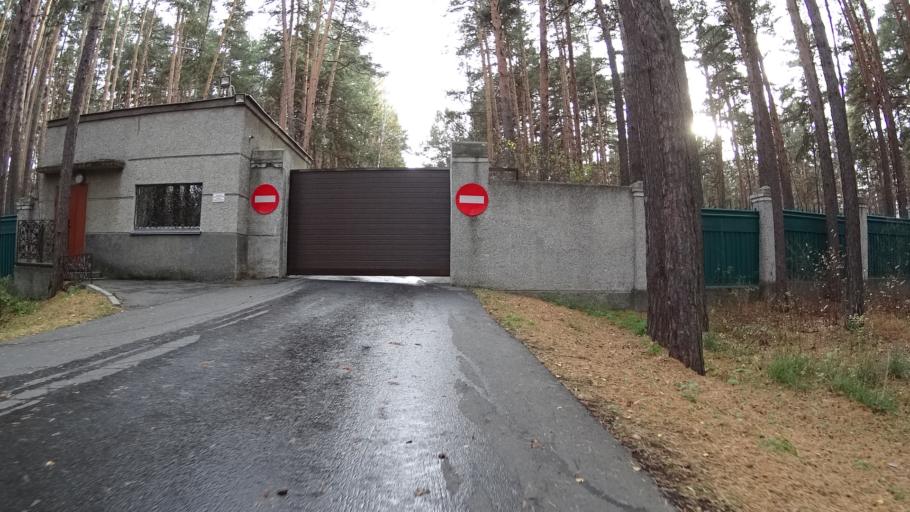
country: RU
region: Chelyabinsk
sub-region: Gorod Chelyabinsk
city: Chelyabinsk
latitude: 55.1385
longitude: 61.3473
